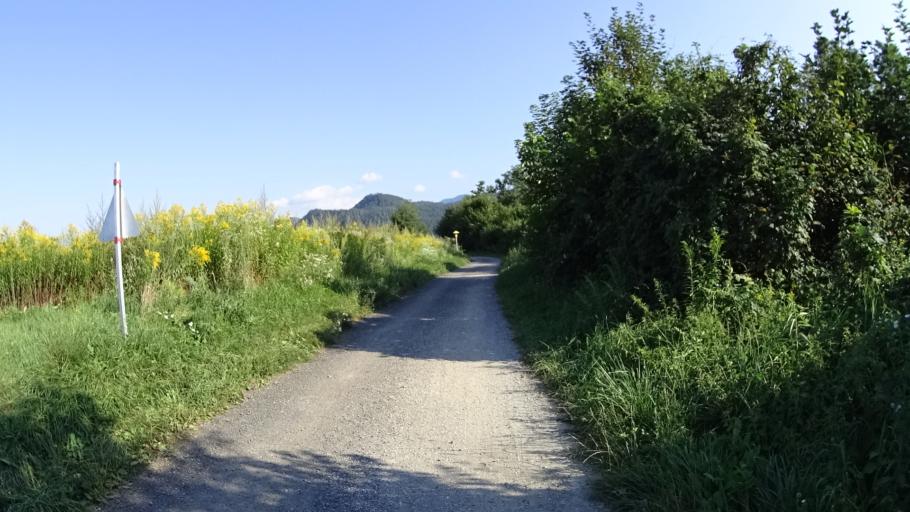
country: AT
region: Carinthia
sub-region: Politischer Bezirk Villach Land
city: Wernberg
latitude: 46.6036
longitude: 13.9458
